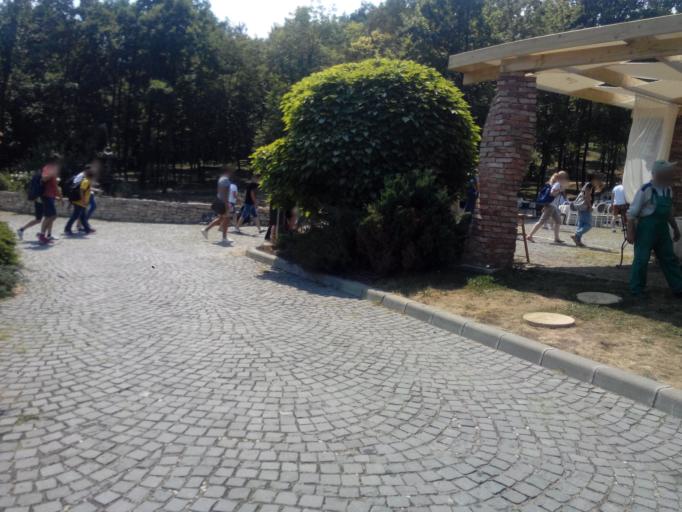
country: RO
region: Cluj
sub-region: Comuna Baciu
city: Mera
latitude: 46.8111
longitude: 23.4860
